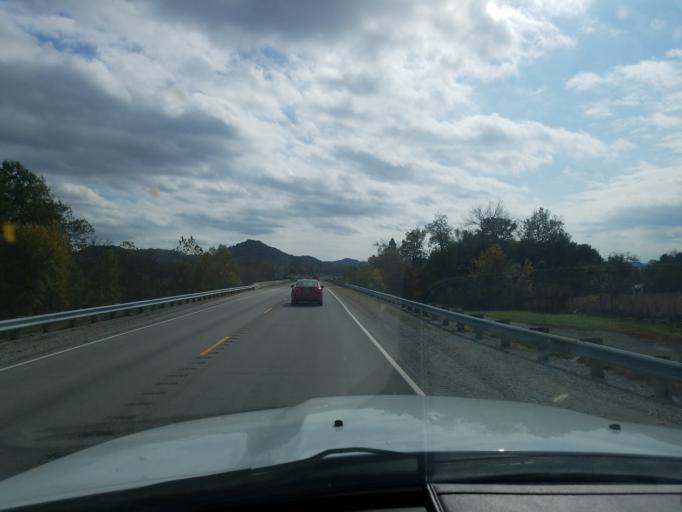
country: US
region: Kentucky
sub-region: Marion County
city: Lebanon
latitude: 37.5091
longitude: -85.2950
